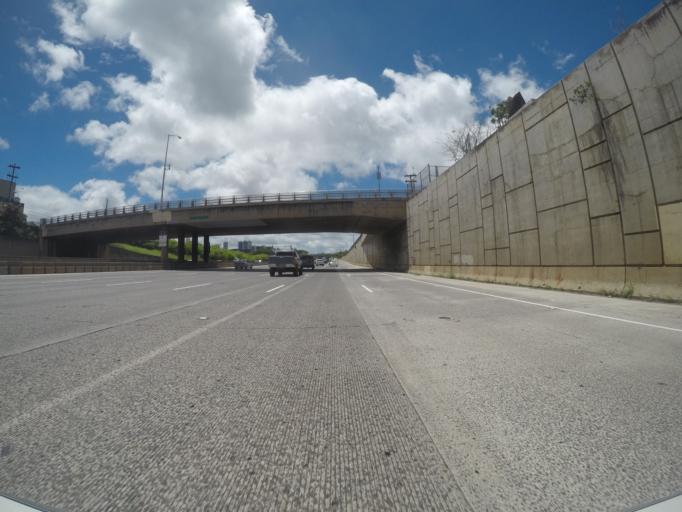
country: US
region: Hawaii
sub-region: Honolulu County
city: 'Aiea
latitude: 21.3797
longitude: -157.9288
